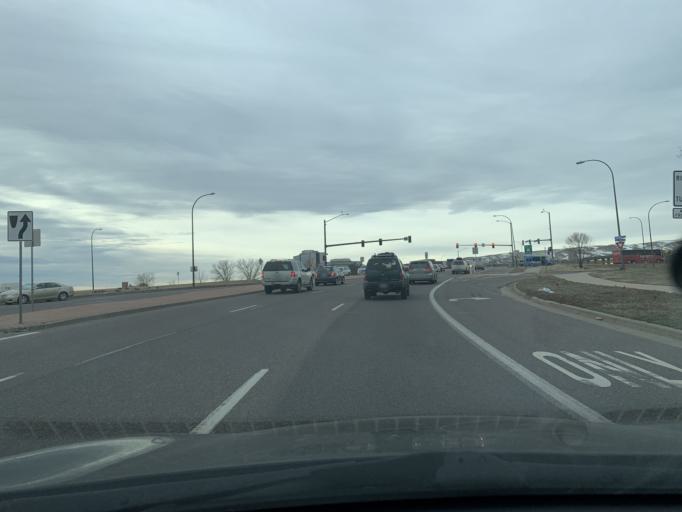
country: US
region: Colorado
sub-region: Jefferson County
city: Applewood
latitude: 39.7270
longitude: -105.1288
